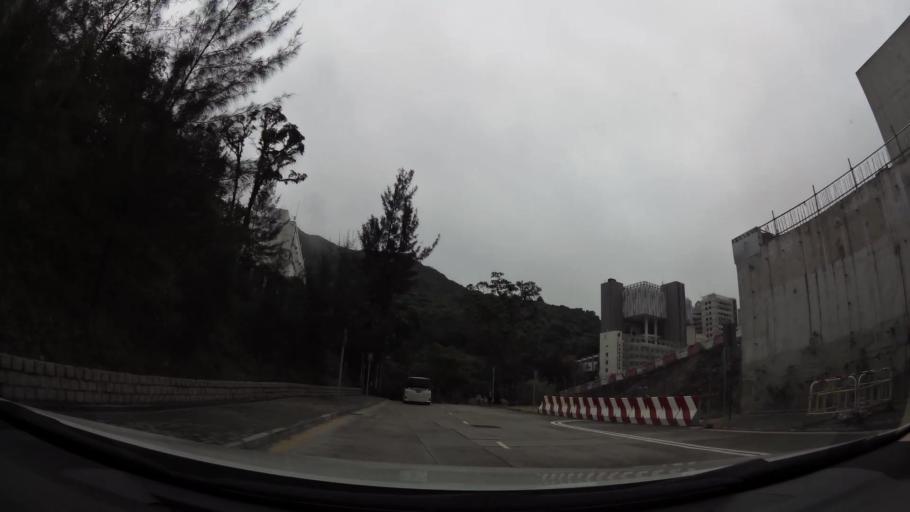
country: HK
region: Wanchai
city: Wan Chai
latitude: 22.2468
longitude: 114.1690
